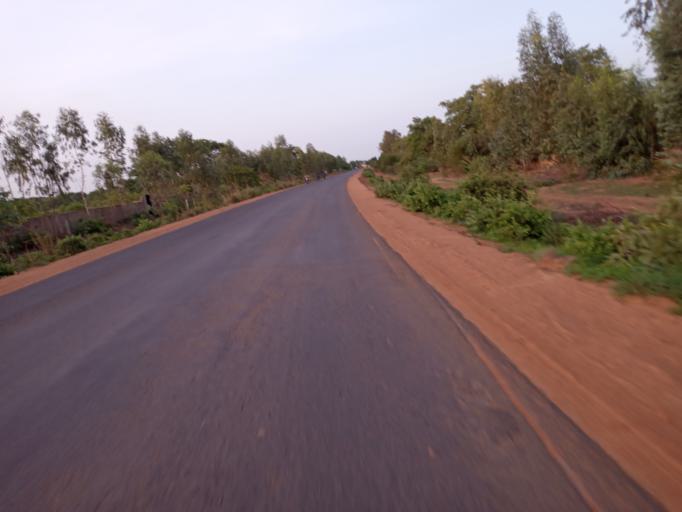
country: ML
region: Bamako
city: Bamako
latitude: 12.2963
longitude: -8.1635
